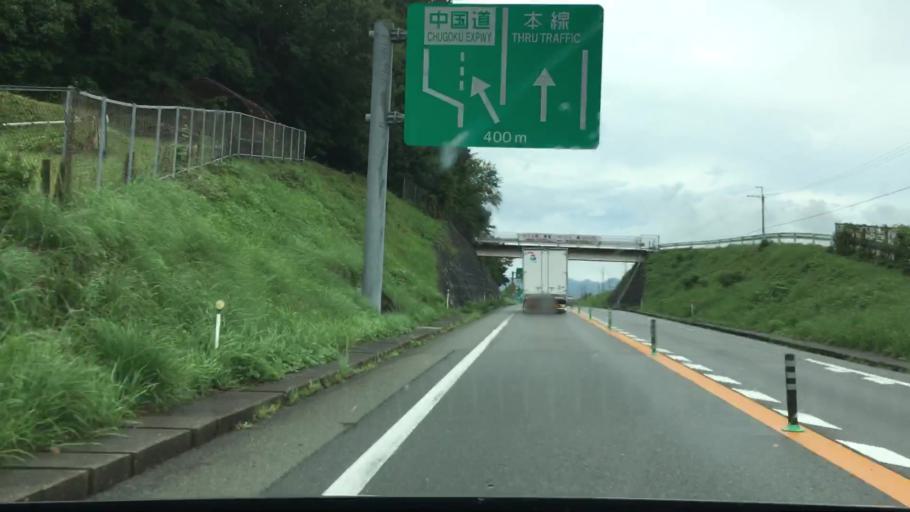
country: JP
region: Hyogo
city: Himeji
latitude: 34.9615
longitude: 134.7697
